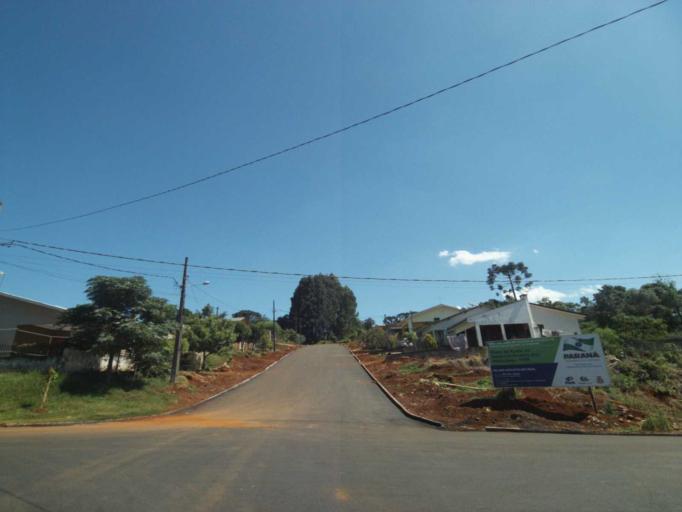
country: BR
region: Parana
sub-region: Laranjeiras Do Sul
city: Laranjeiras do Sul
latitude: -25.3808
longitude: -52.2071
